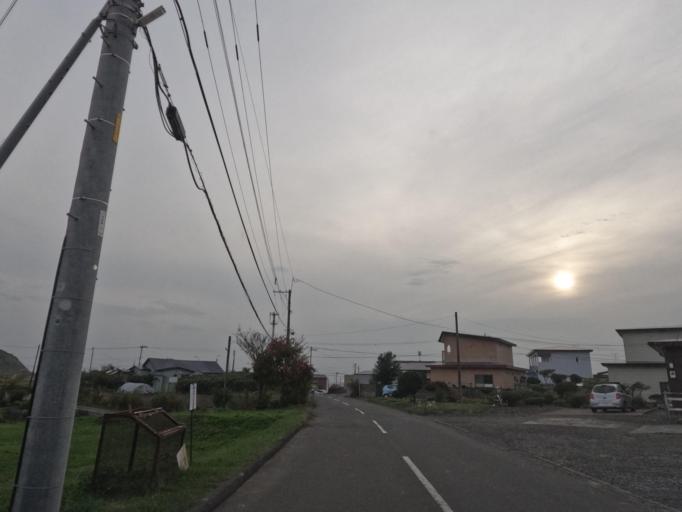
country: JP
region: Hokkaido
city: Date
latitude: 42.3861
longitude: 140.9109
